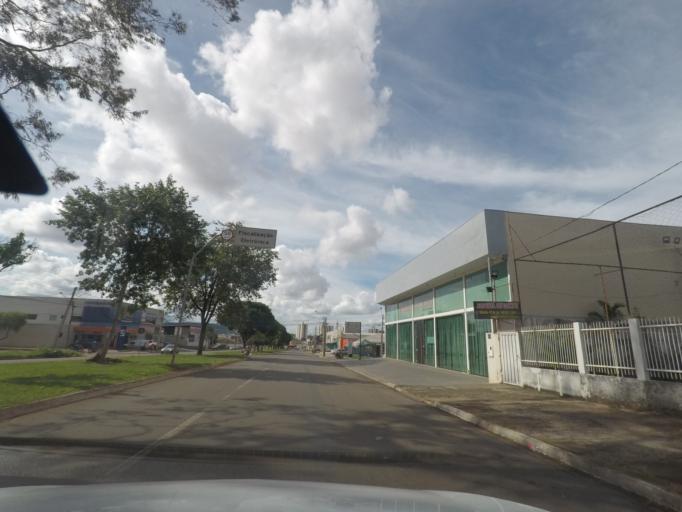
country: BR
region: Goias
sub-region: Goiania
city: Goiania
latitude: -16.7026
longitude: -49.3264
